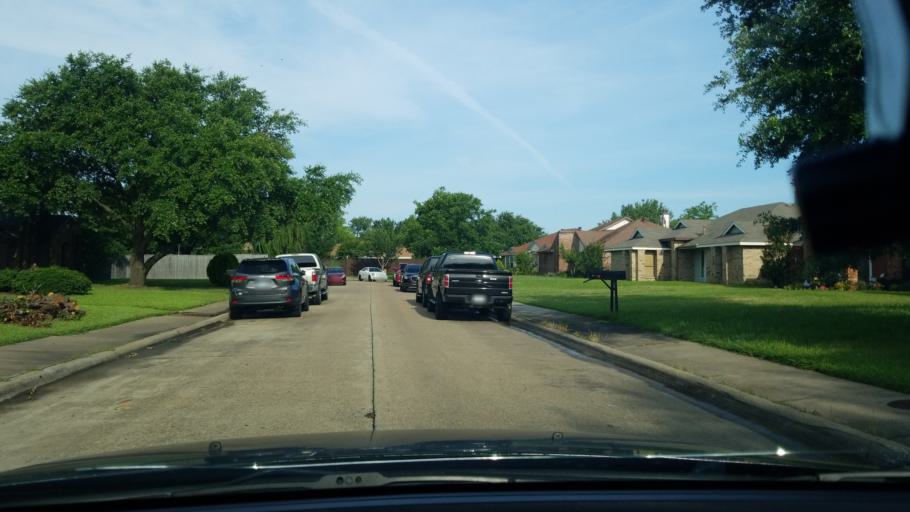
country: US
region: Texas
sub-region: Dallas County
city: Mesquite
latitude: 32.8028
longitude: -96.6068
